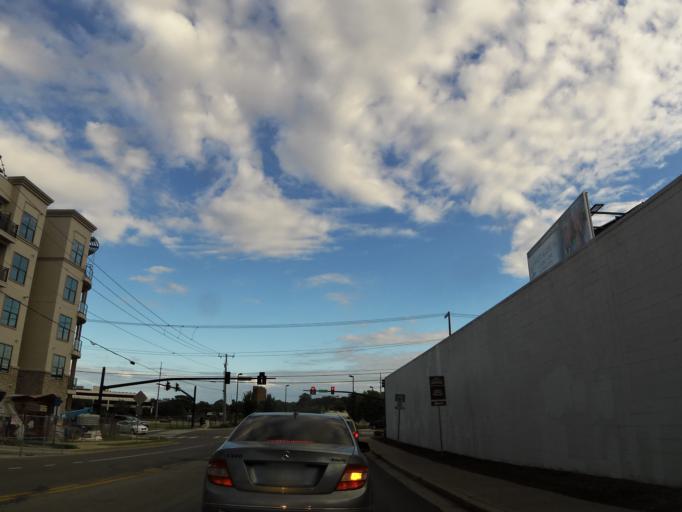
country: US
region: Tennessee
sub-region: Davidson County
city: Nashville
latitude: 36.1546
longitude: -86.8184
